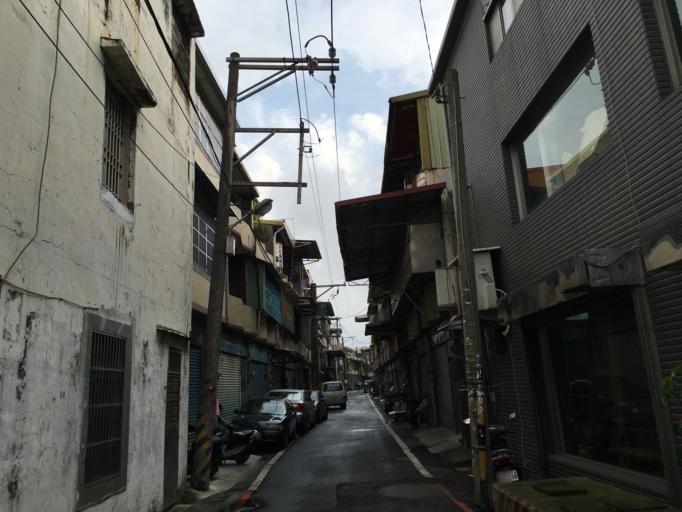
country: TW
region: Taiwan
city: Daxi
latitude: 24.8731
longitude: 121.2309
